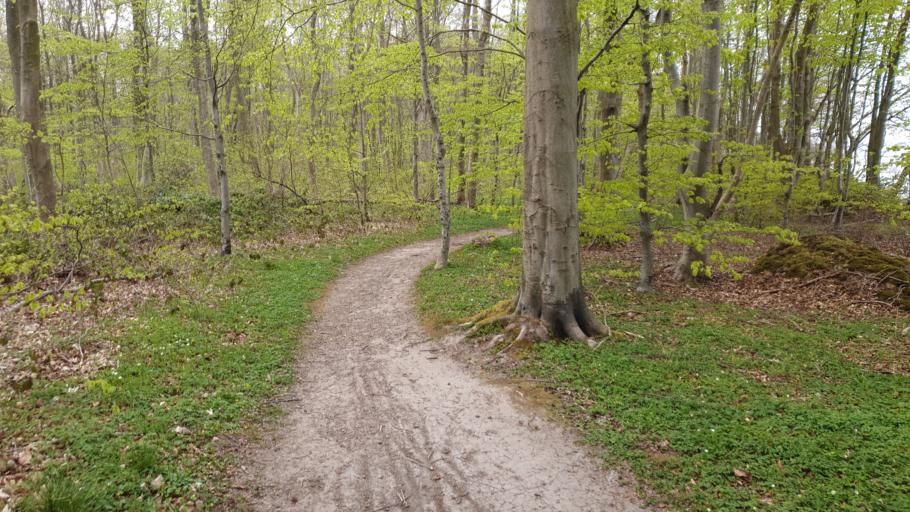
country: DK
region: South Denmark
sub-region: Sonderborg Kommune
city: Dybbol
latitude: 54.8516
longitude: 9.7601
